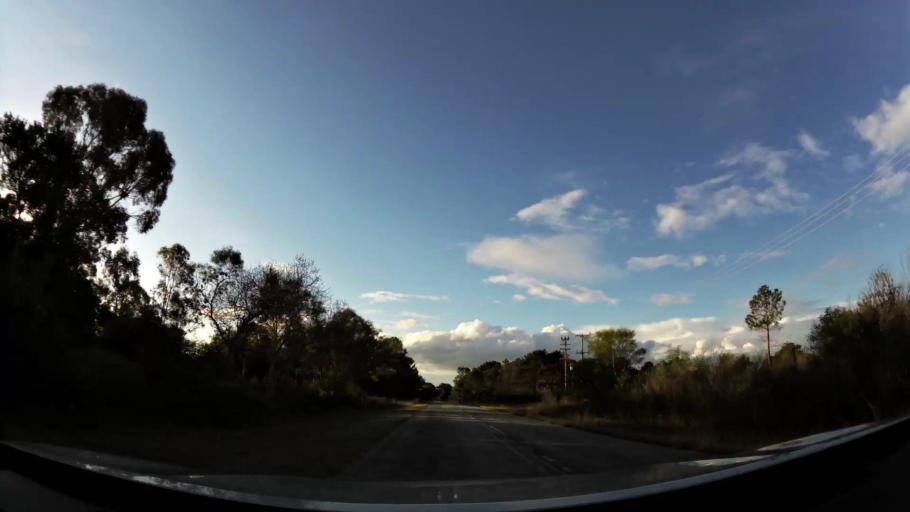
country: ZA
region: Eastern Cape
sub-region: Nelson Mandela Bay Metropolitan Municipality
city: Port Elizabeth
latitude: -33.9785
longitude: 25.4837
